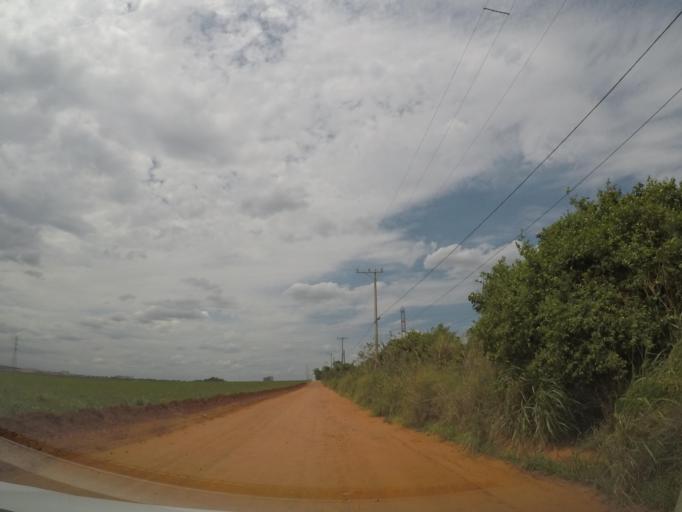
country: BR
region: Sao Paulo
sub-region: Sumare
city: Sumare
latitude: -22.8420
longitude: -47.2927
